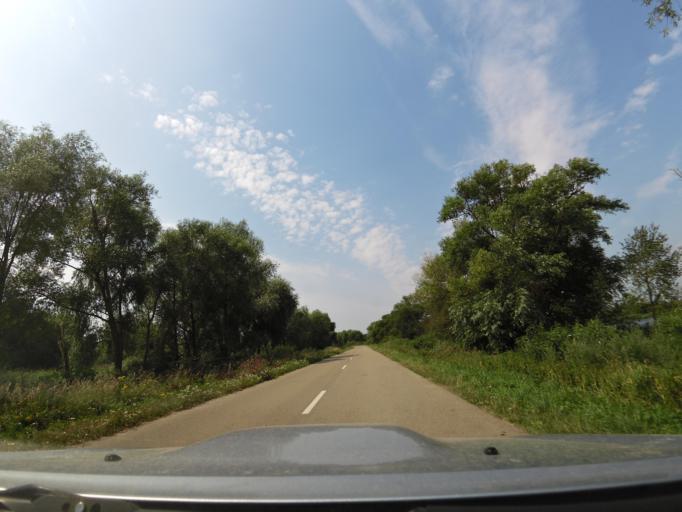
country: LT
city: Rusne
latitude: 55.3436
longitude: 21.3338
